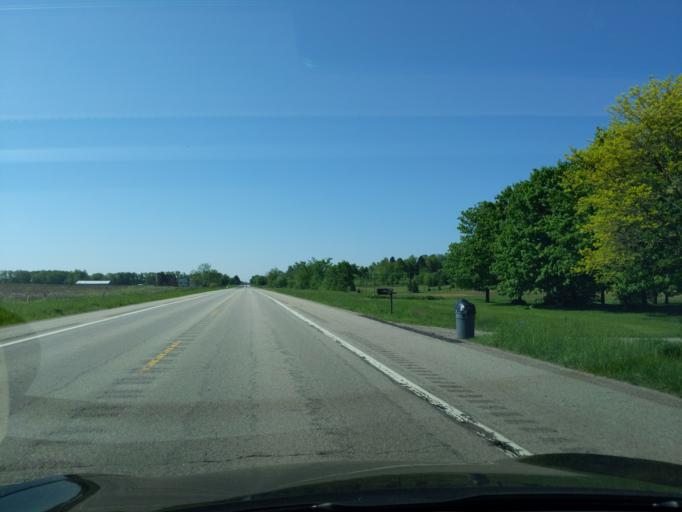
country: US
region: Michigan
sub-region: Ingham County
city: Stockbridge
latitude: 42.5376
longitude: -84.1912
